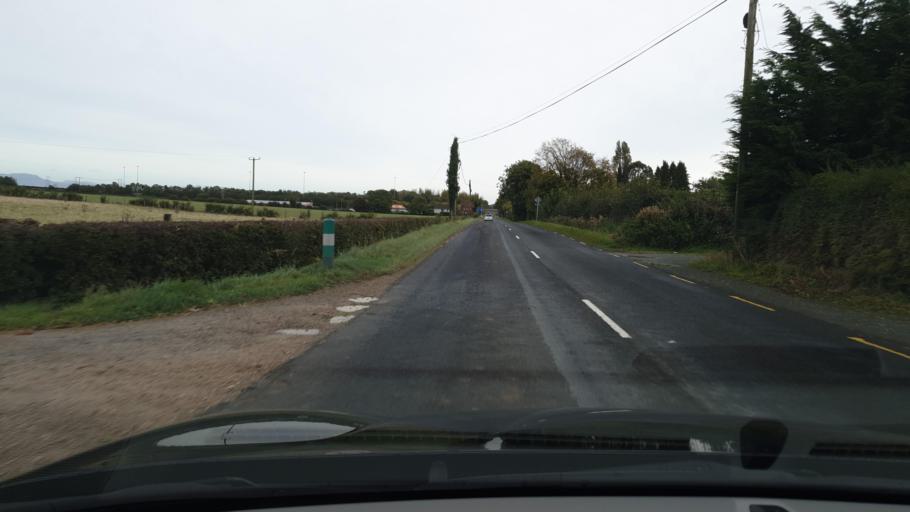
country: IE
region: Leinster
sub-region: Lu
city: Dunleer
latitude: 53.8182
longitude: -6.4111
